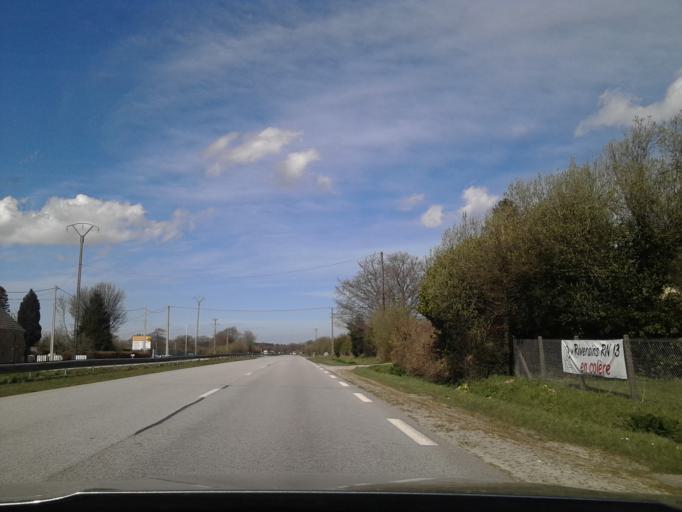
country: FR
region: Lower Normandy
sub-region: Departement de la Manche
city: Brix
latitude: 49.5713
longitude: -1.5759
